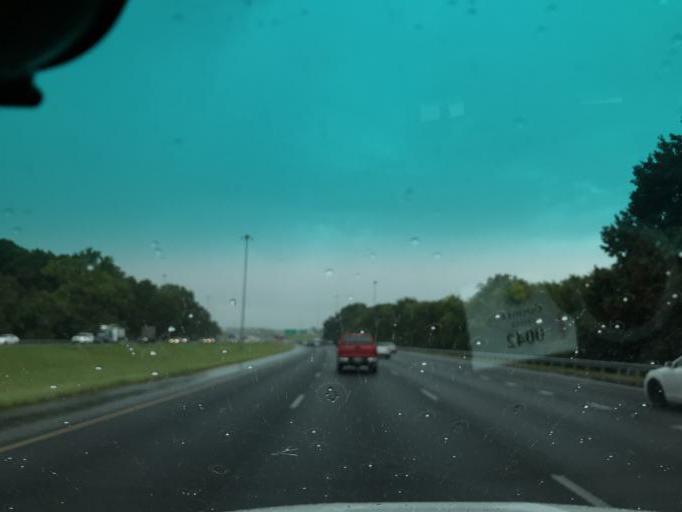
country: US
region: Alabama
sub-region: Montgomery County
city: Montgomery
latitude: 32.3586
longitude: -86.2524
